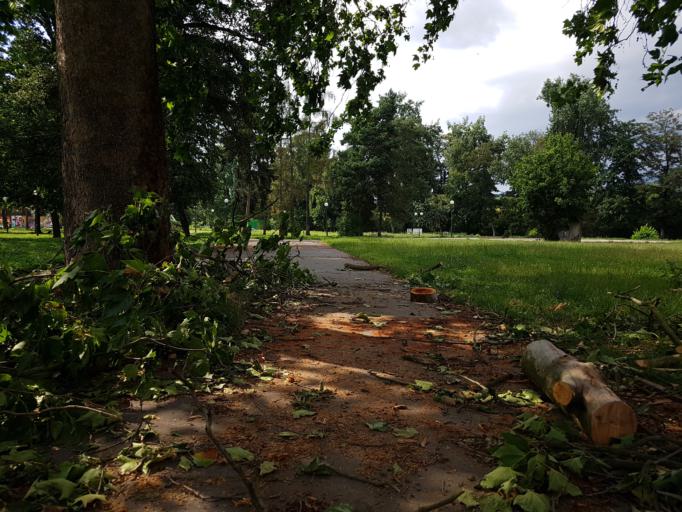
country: CZ
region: Praha
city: Prague
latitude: 50.1088
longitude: 14.4299
